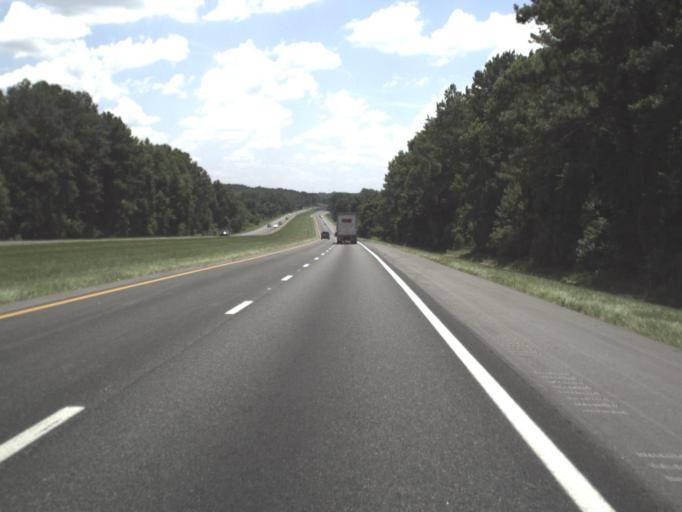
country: US
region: Florida
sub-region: Madison County
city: Madison
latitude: 30.4351
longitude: -83.4865
